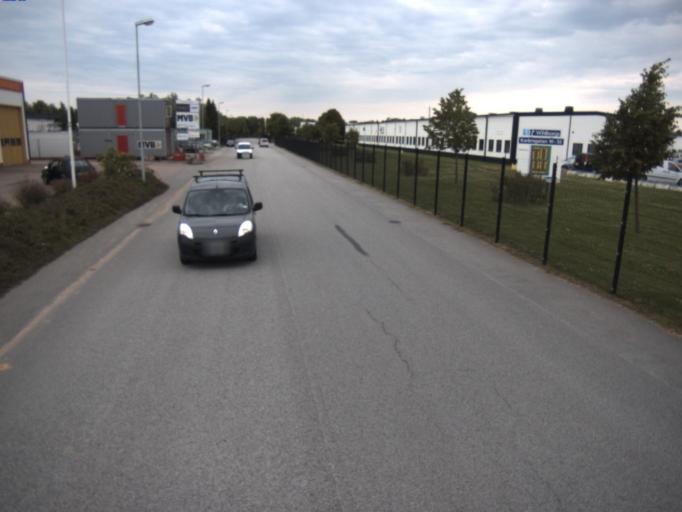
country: SE
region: Skane
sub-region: Helsingborg
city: Odakra
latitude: 56.0833
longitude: 12.7350
